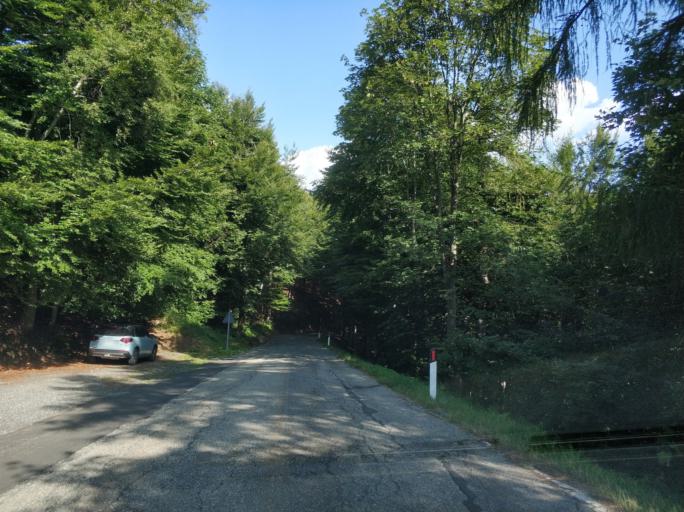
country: IT
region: Piedmont
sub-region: Provincia di Torino
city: Rubiana
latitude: 45.1792
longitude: 7.3809
